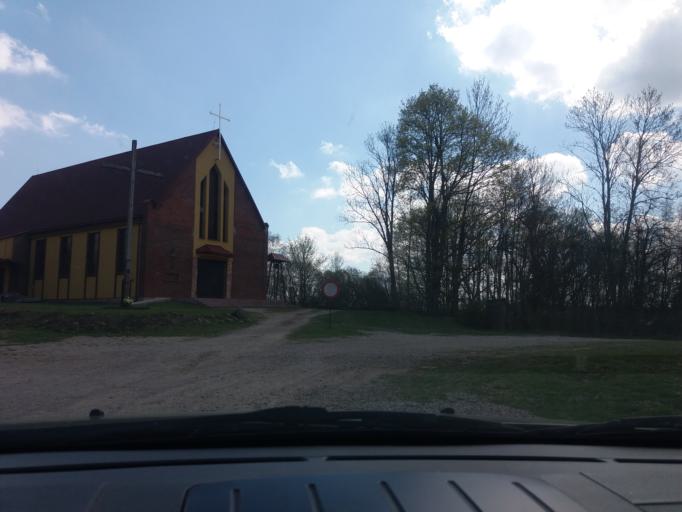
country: PL
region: Warmian-Masurian Voivodeship
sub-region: Powiat nidzicki
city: Nidzica
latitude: 53.3749
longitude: 20.6067
